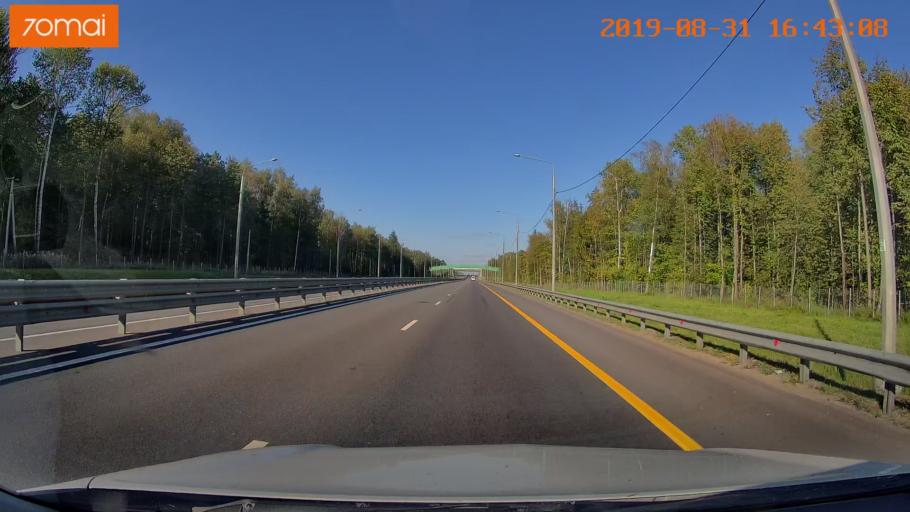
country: RU
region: Kaluga
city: Mstikhino
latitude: 54.6048
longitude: 36.0988
